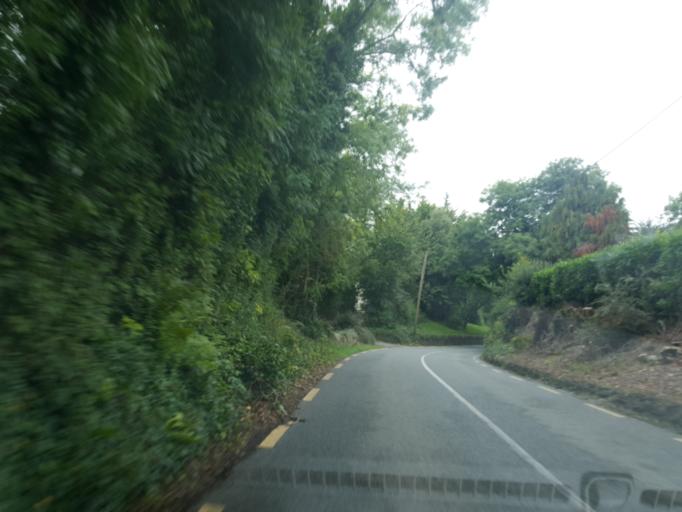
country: IE
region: Leinster
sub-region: Wicklow
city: Valleymount
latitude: 53.1224
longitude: -6.6355
